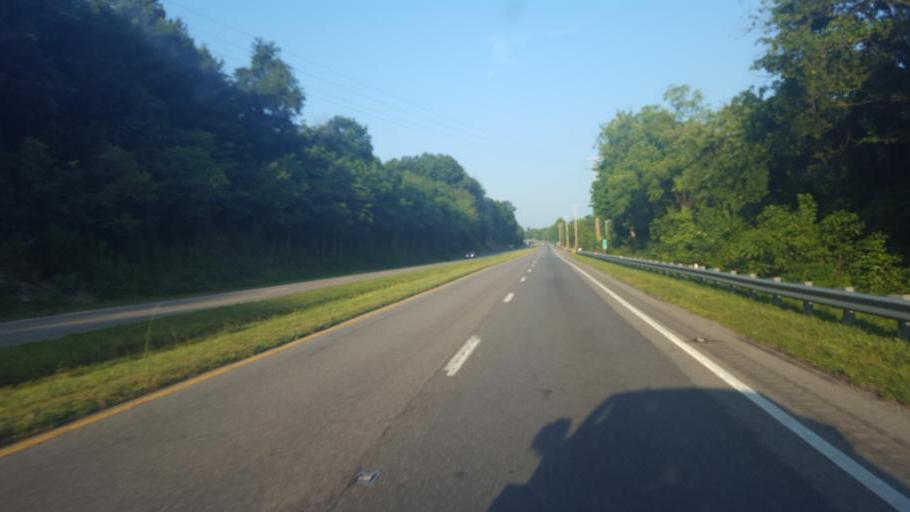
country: US
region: Tennessee
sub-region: Hawkins County
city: Mount Carmel
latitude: 36.6422
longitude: -82.7294
